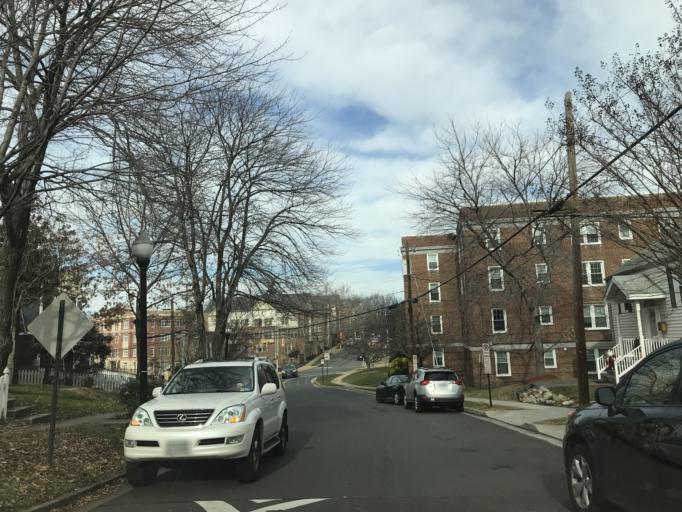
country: US
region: Virginia
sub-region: Arlington County
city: Arlington
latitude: 38.8939
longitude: -77.0929
